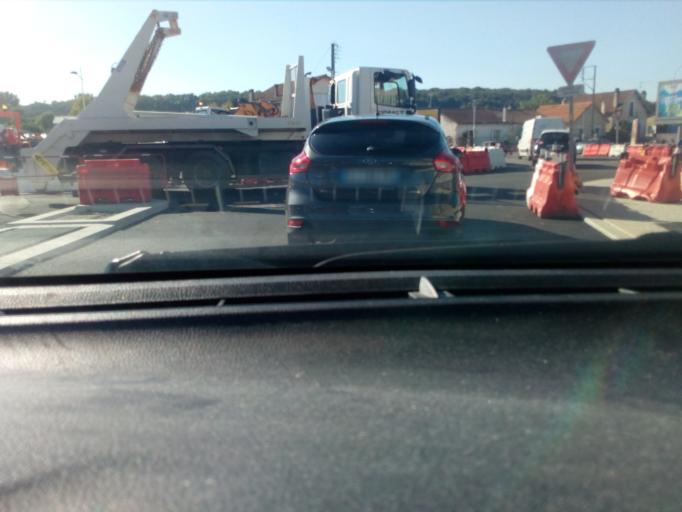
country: FR
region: Poitou-Charentes
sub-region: Departement de la Charente
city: Angouleme
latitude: 45.6434
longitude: 0.1357
